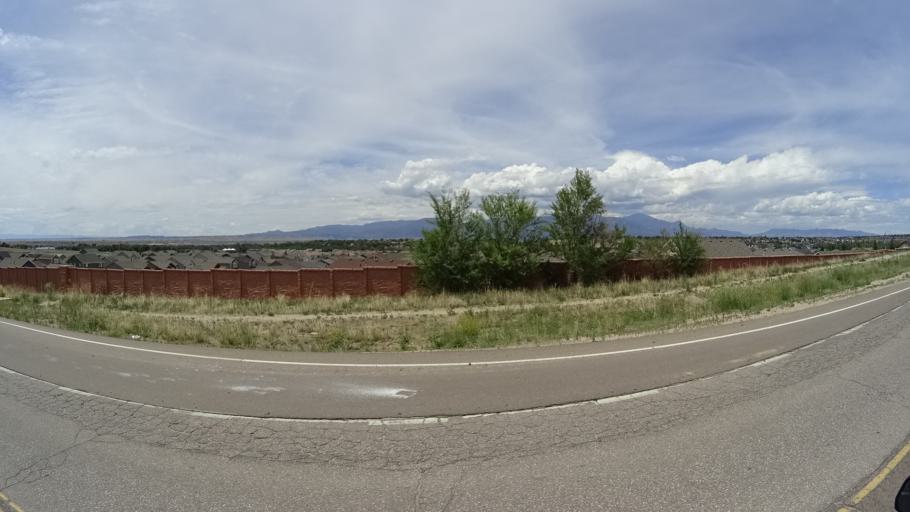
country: US
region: Colorado
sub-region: El Paso County
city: Fountain
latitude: 38.6922
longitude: -104.6736
